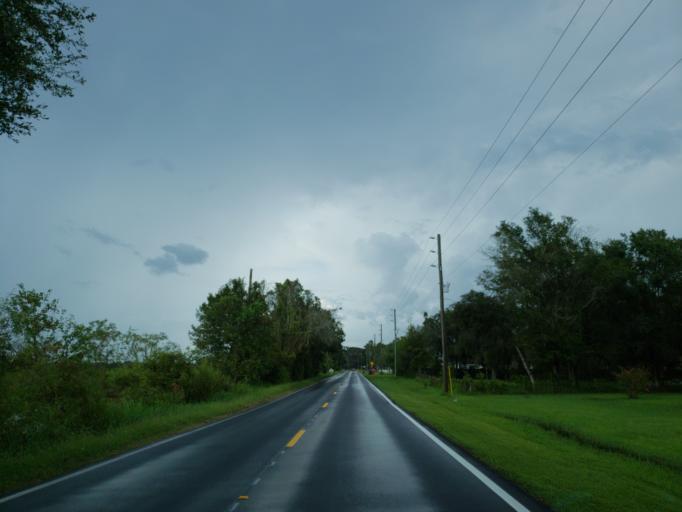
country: US
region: Florida
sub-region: Pasco County
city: Land O' Lakes
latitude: 28.2907
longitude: -82.4333
